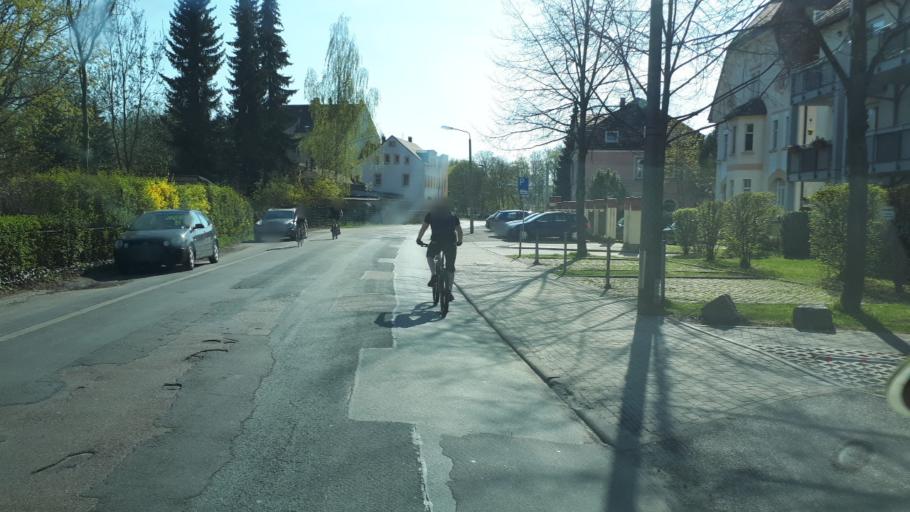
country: DE
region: Saxony
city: Chemnitz
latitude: 50.7926
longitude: 12.9280
